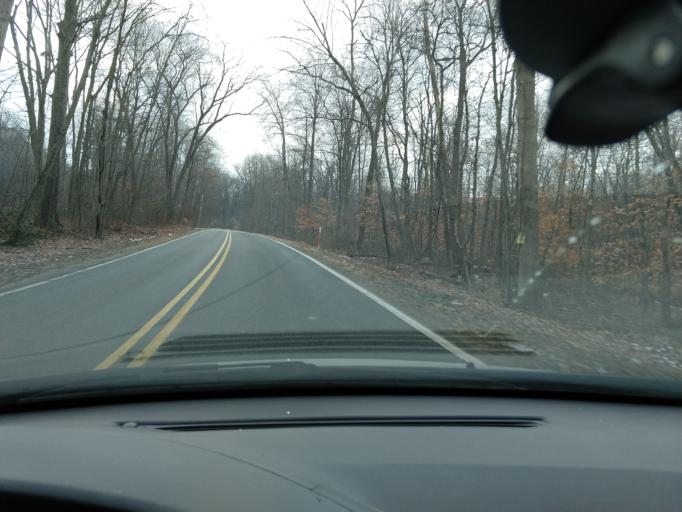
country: US
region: Pennsylvania
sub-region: Berks County
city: Birdsboro
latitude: 40.2404
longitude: -75.7751
